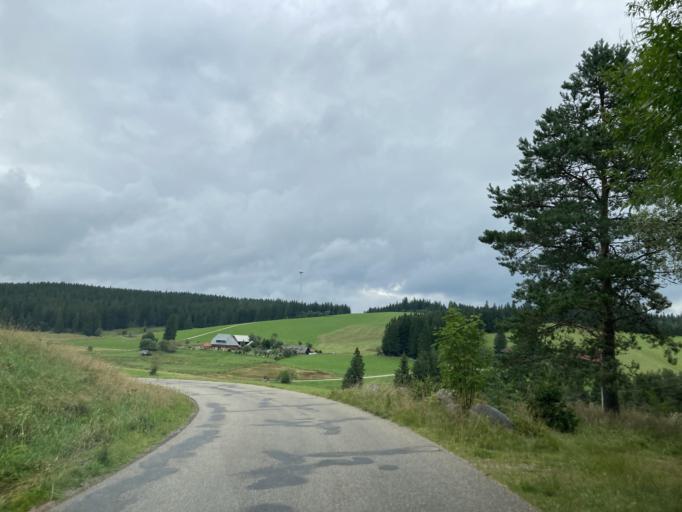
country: DE
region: Baden-Wuerttemberg
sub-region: Freiburg Region
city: Schonwald im Schwarzwald
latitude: 48.1162
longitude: 8.1982
